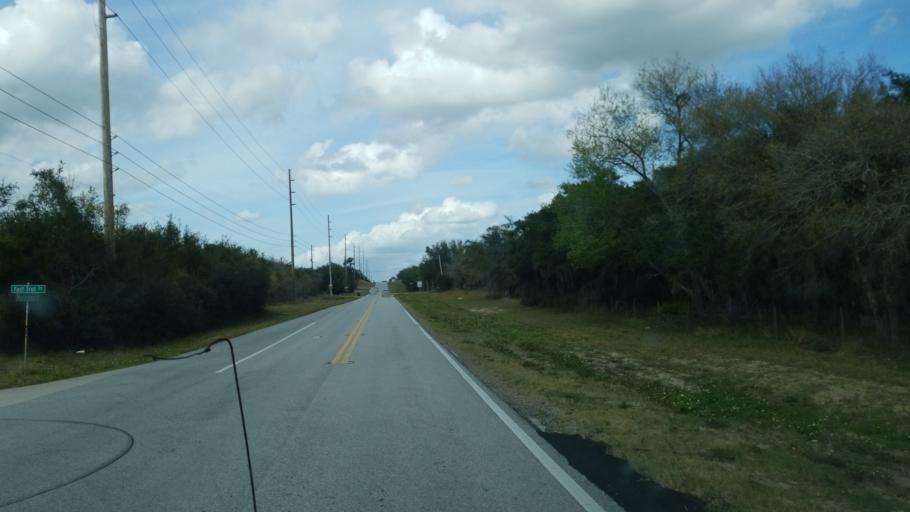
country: US
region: Florida
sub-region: Polk County
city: Lake Wales
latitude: 27.9528
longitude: -81.5378
